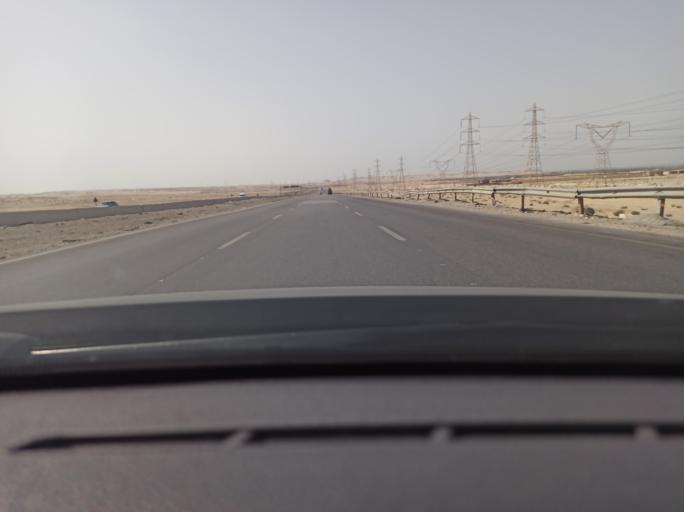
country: EG
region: Muhafazat al Qahirah
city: Halwan
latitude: 29.7418
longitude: 31.4097
